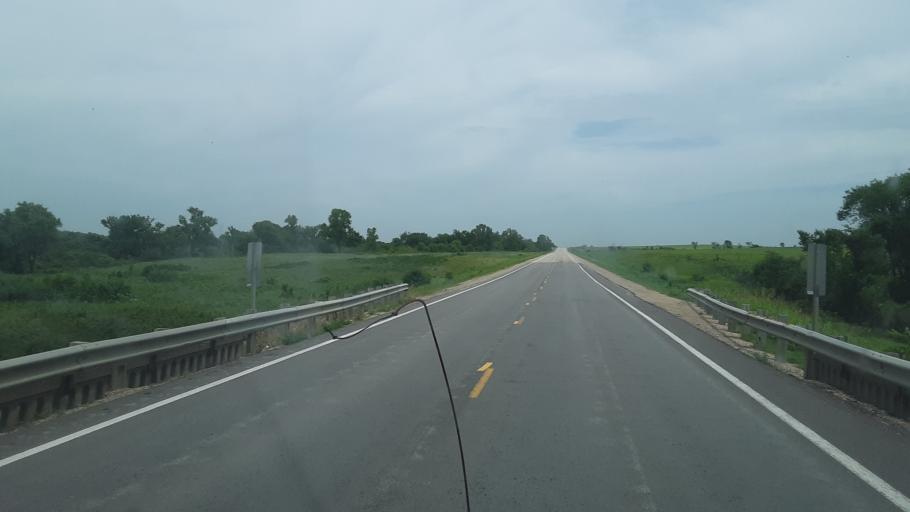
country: US
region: Kansas
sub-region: Woodson County
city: Yates Center
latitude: 37.8464
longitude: -95.8358
